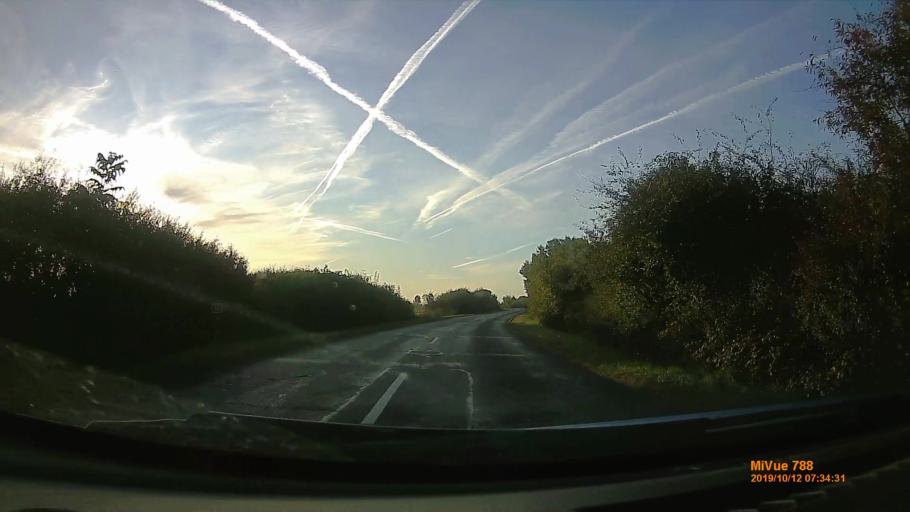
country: HU
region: Hajdu-Bihar
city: Pocsaj
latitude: 47.2614
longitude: 21.8060
